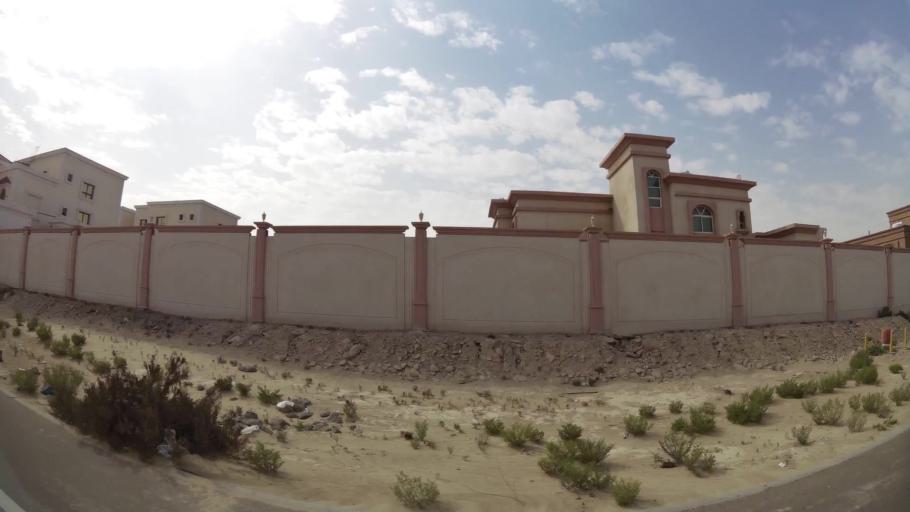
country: AE
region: Abu Dhabi
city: Abu Dhabi
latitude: 24.2765
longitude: 54.6638
